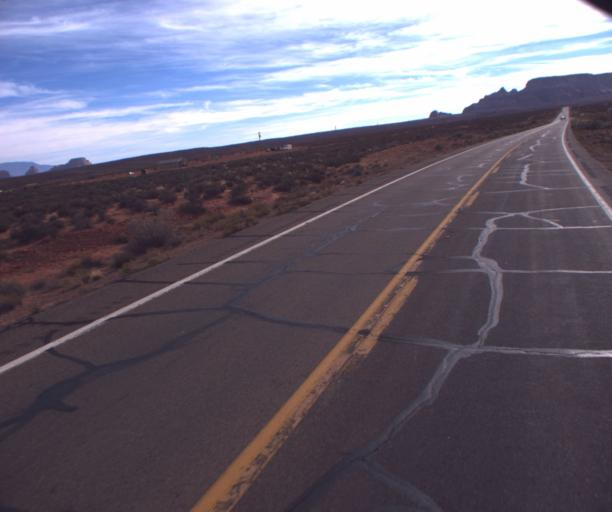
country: US
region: Arizona
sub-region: Coconino County
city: LeChee
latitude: 36.8910
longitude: -111.3707
